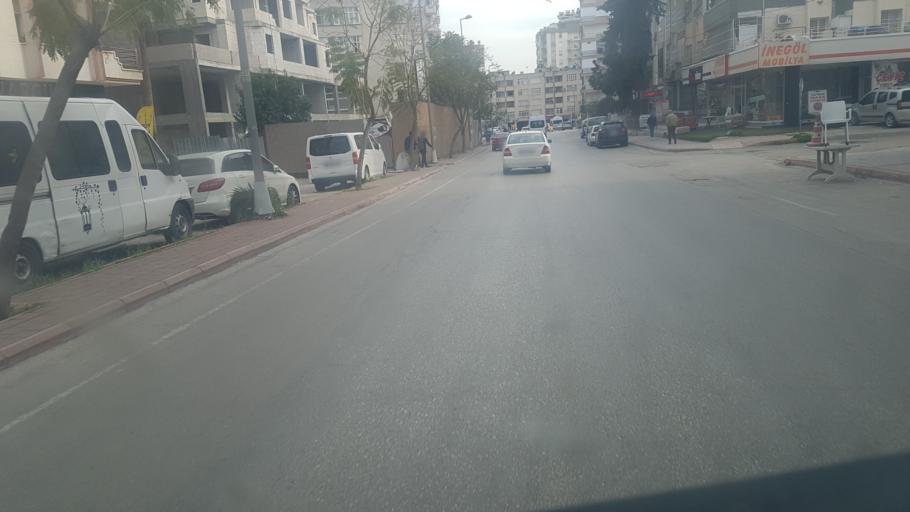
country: TR
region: Adana
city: Adana
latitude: 37.0284
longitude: 35.3104
